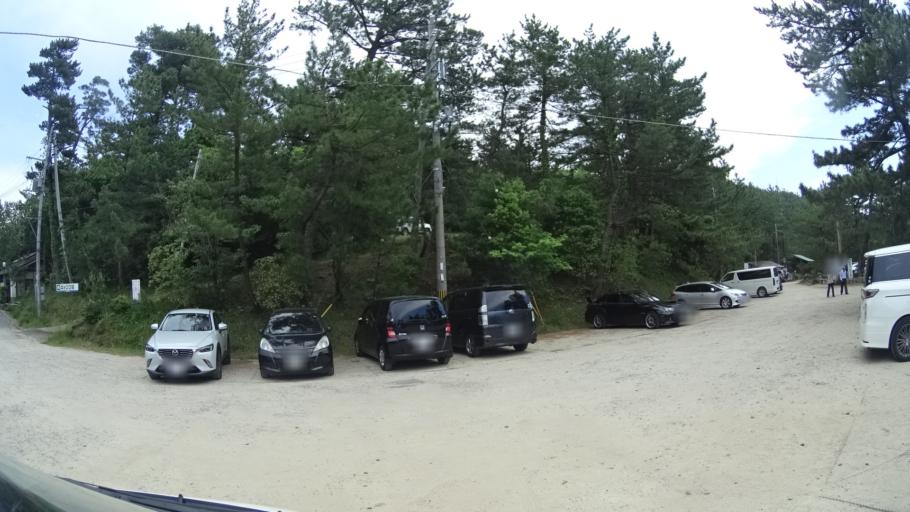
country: JP
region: Kyoto
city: Miyazu
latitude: 35.7018
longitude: 135.0462
